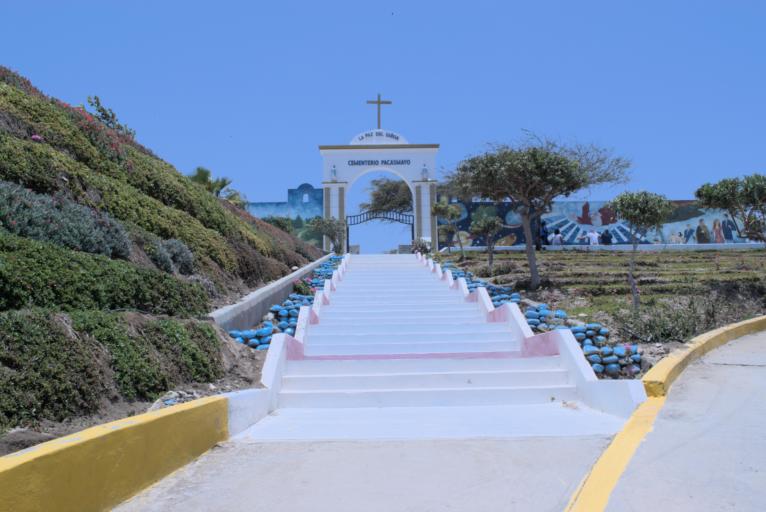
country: PE
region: La Libertad
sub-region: Provincia de Pacasmayo
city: Pacasmayo
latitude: -7.4003
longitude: -79.5711
